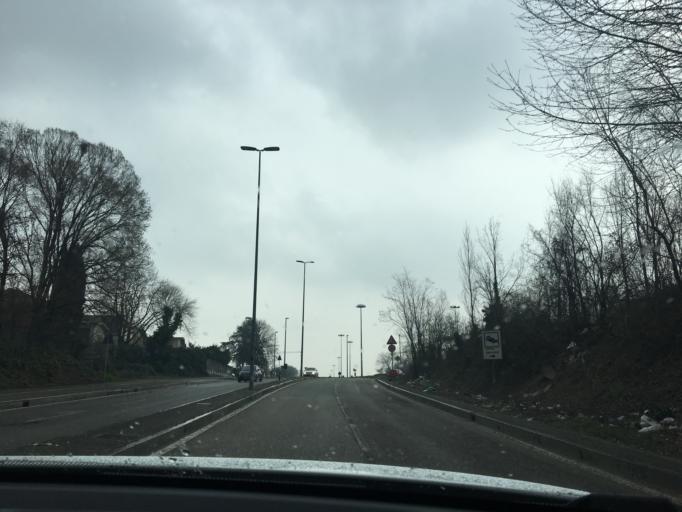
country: IT
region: Piedmont
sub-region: Provincia di Torino
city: Grugliasco
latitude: 45.0434
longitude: 7.5899
